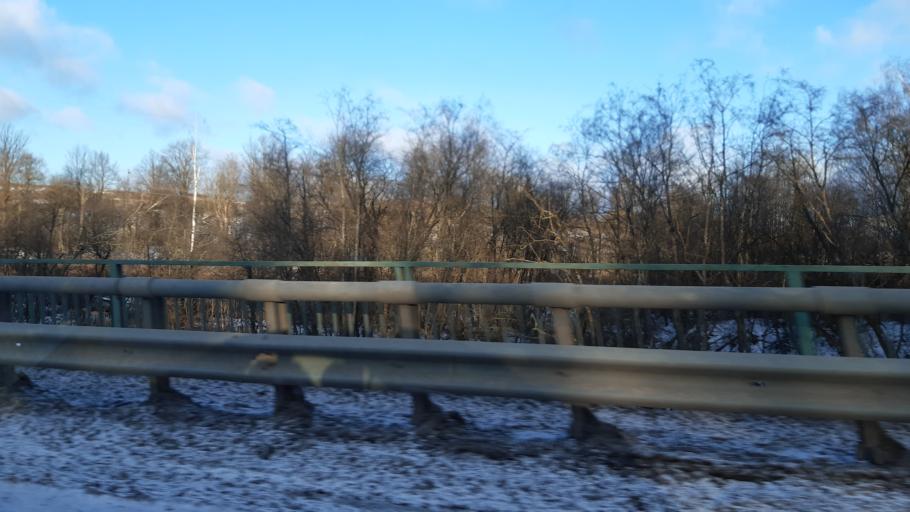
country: RU
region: Vladimir
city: Arsaki
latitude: 56.2827
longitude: 38.3980
